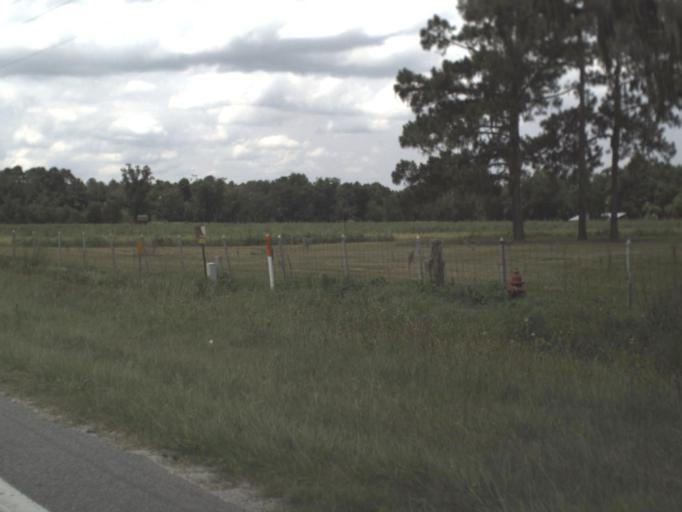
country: US
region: Florida
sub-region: Hamilton County
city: Jasper
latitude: 30.4901
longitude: -82.9305
